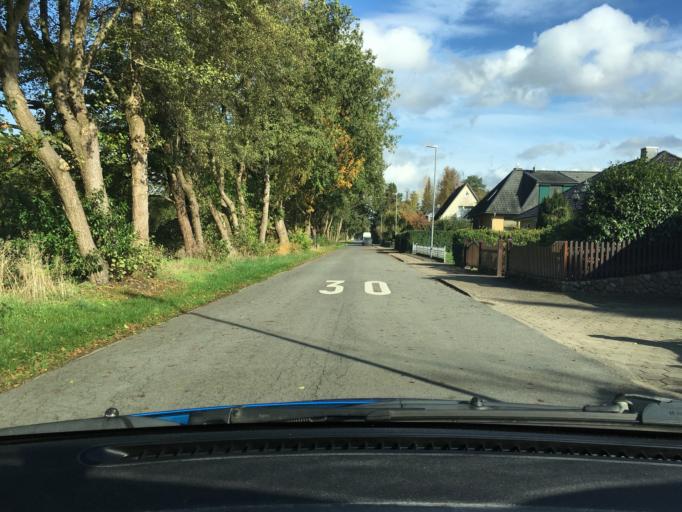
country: DE
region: Lower Saxony
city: Kakenstorf
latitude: 53.3147
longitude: 9.7883
